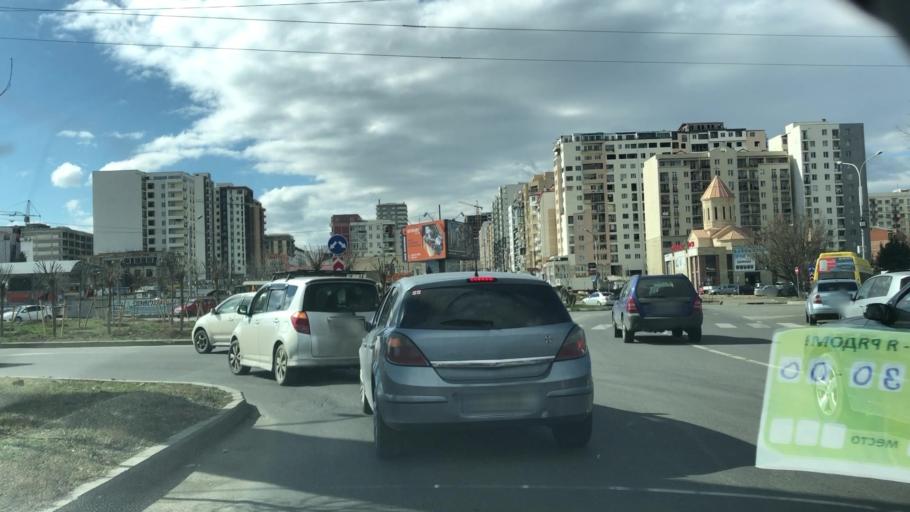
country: GE
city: Zahesi
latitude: 41.7873
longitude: 44.7655
